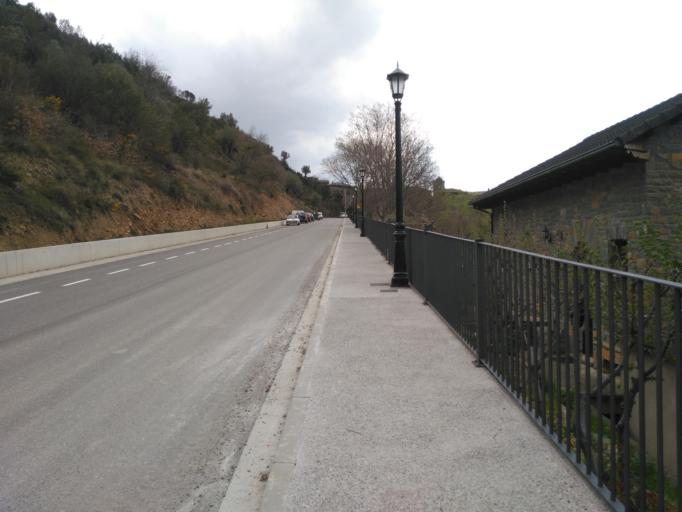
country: ES
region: Aragon
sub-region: Provincia de Huesca
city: Boltana
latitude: 42.4489
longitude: 0.0661
